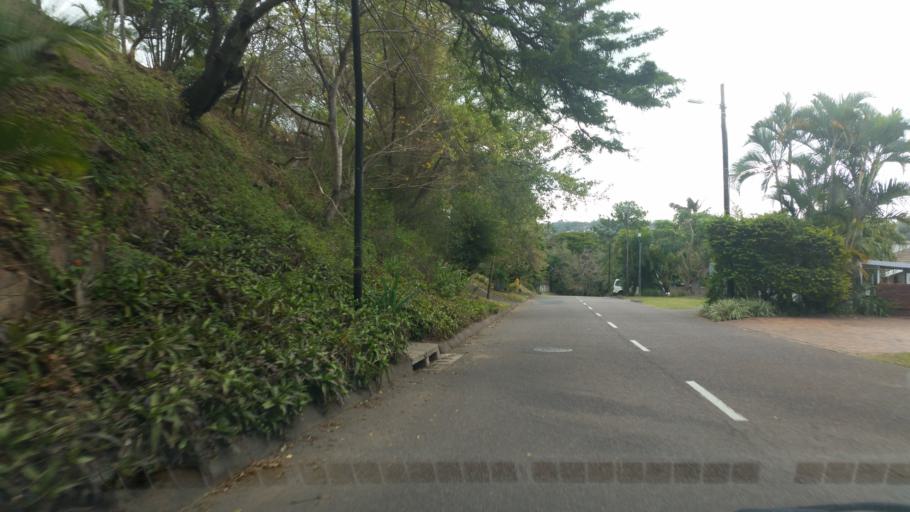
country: ZA
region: KwaZulu-Natal
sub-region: eThekwini Metropolitan Municipality
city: Berea
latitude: -29.8234
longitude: 30.9379
